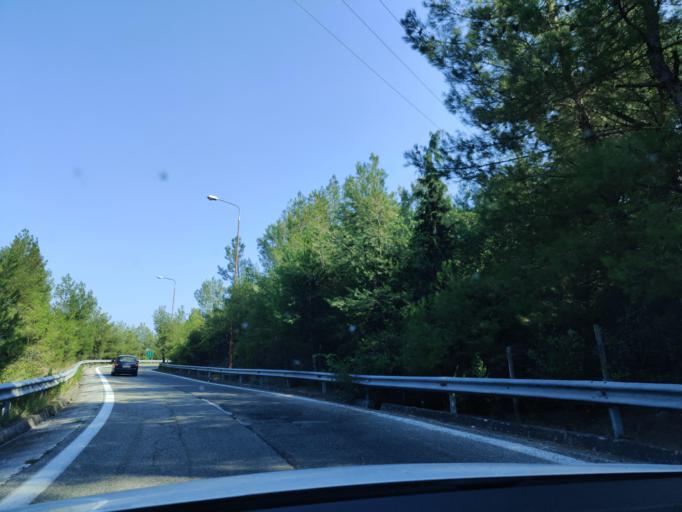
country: GR
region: East Macedonia and Thrace
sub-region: Nomos Kavalas
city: Amygdaleonas
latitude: 40.9408
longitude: 24.3742
